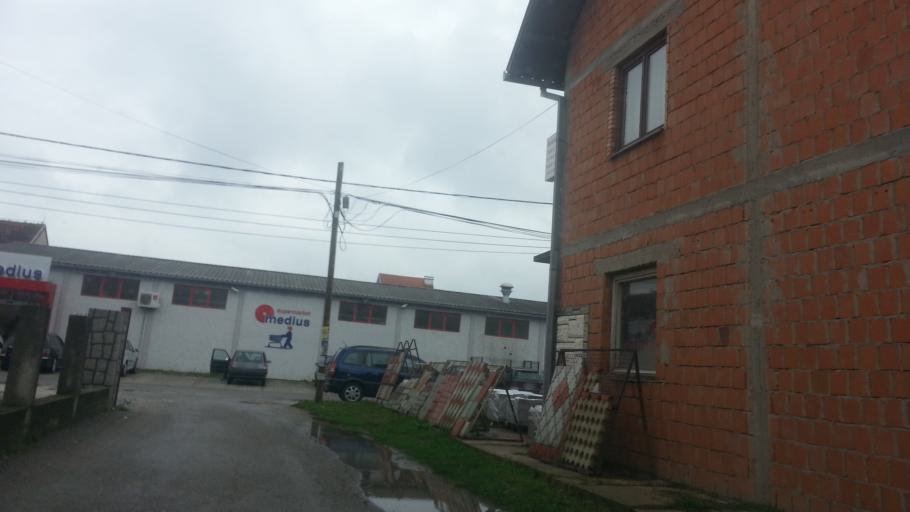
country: RS
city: Novi Banovci
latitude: 44.9096
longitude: 20.2877
